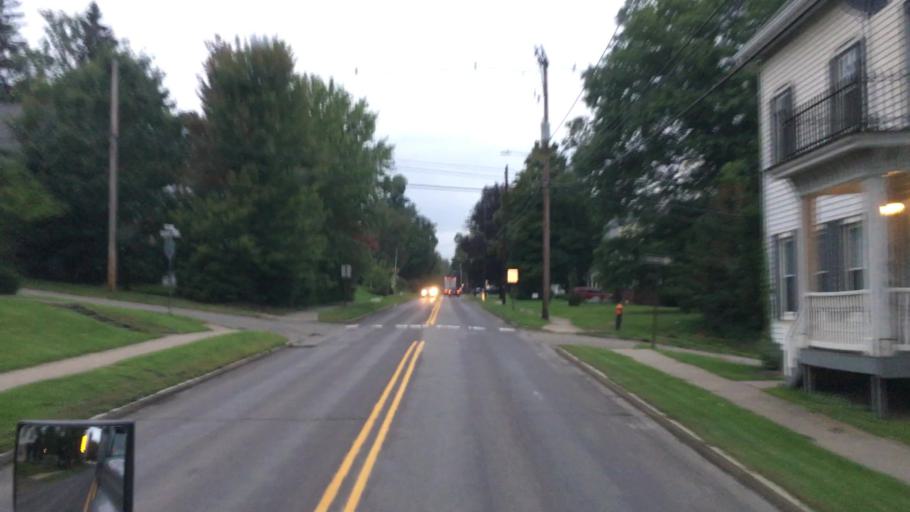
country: US
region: Pennsylvania
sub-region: Bradford County
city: Towanda
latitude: 41.7724
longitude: -76.4438
